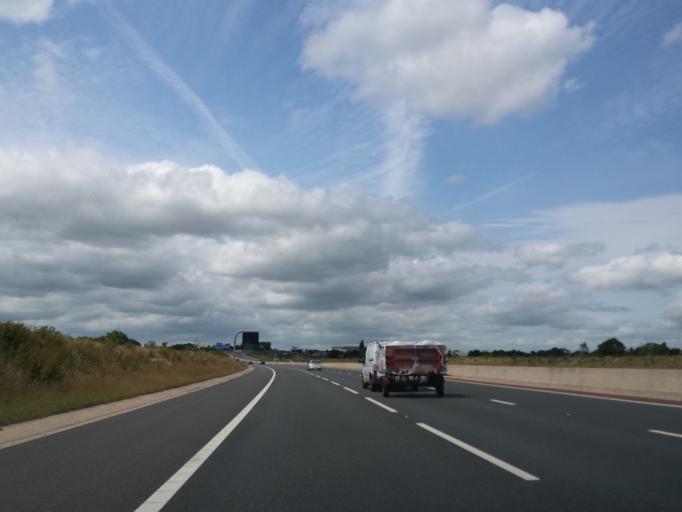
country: GB
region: England
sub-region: North Yorkshire
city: Bedale
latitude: 54.2953
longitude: -1.5553
